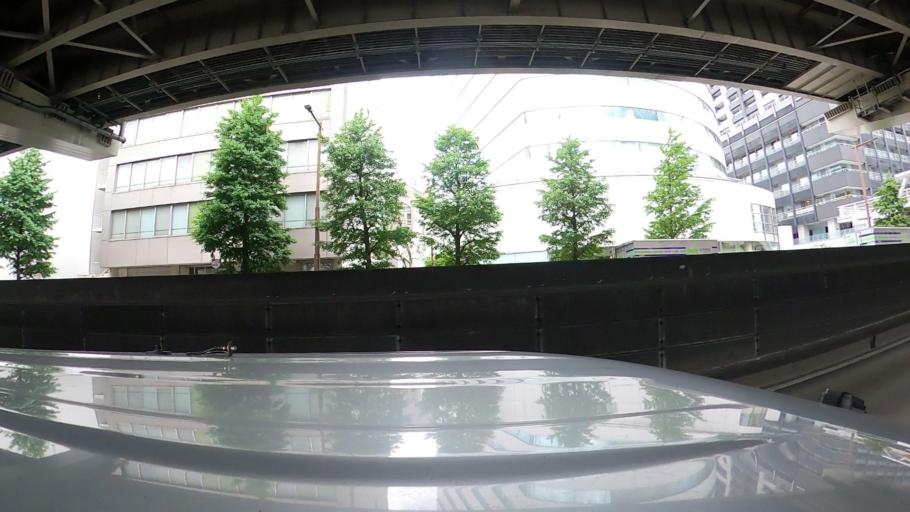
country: JP
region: Kanagawa
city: Yokohama
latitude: 35.4620
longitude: 139.6254
